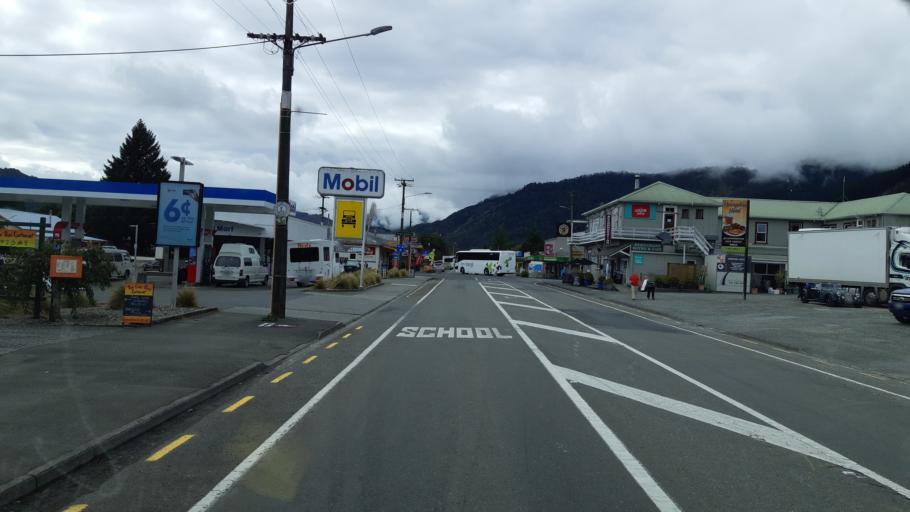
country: NZ
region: West Coast
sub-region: Buller District
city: Westport
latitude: -41.8001
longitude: 172.3238
